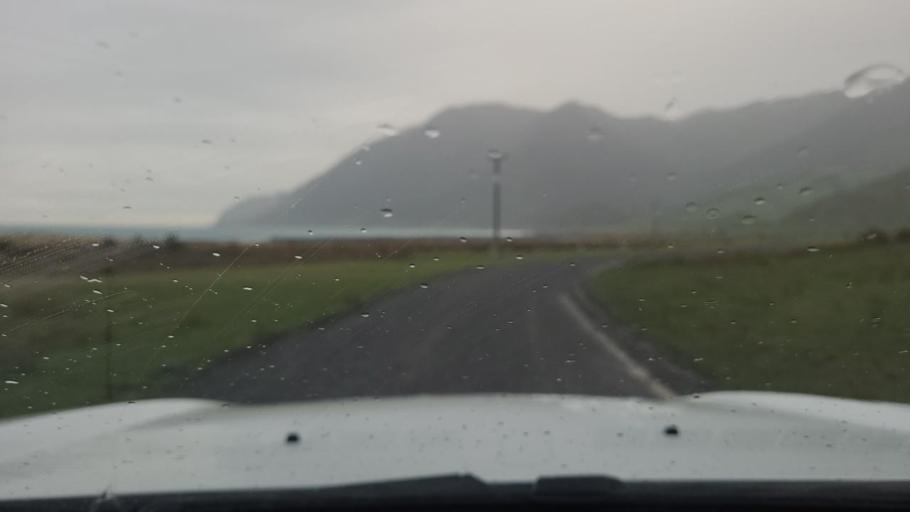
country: NZ
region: Wellington
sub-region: South Wairarapa District
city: Waipawa
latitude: -41.5672
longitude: 175.3947
